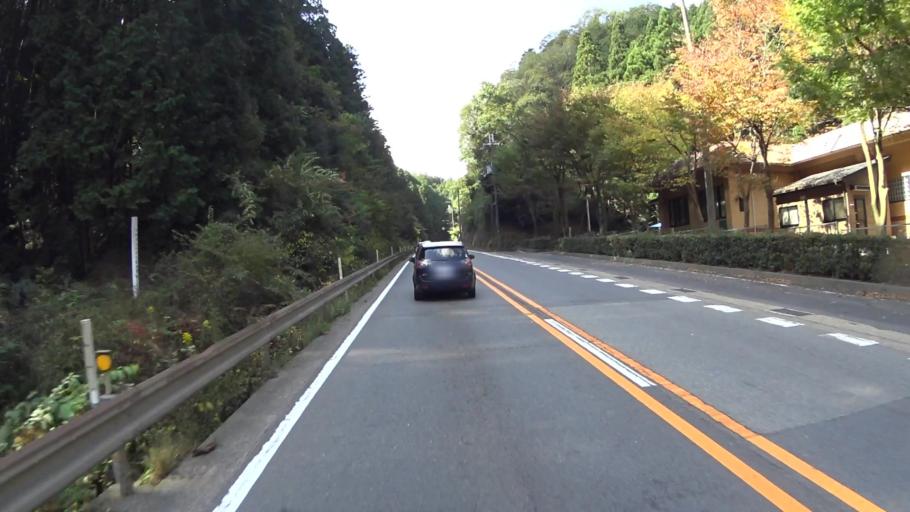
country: JP
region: Kyoto
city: Kameoka
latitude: 34.9924
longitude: 135.6445
